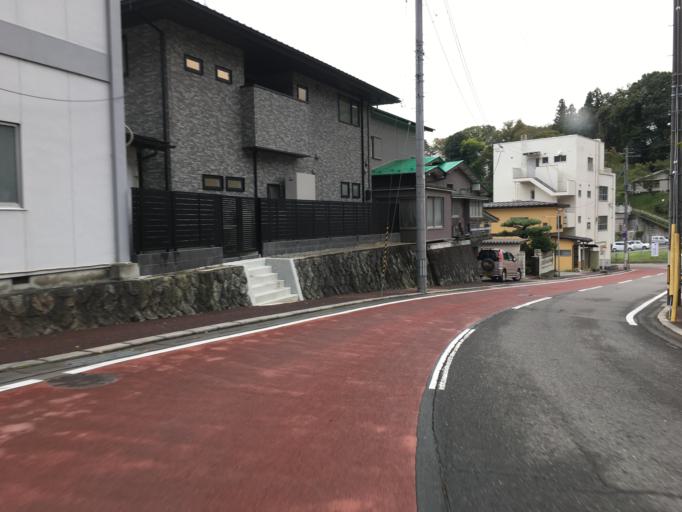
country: JP
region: Fukushima
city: Nihommatsu
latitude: 37.5943
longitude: 140.4405
